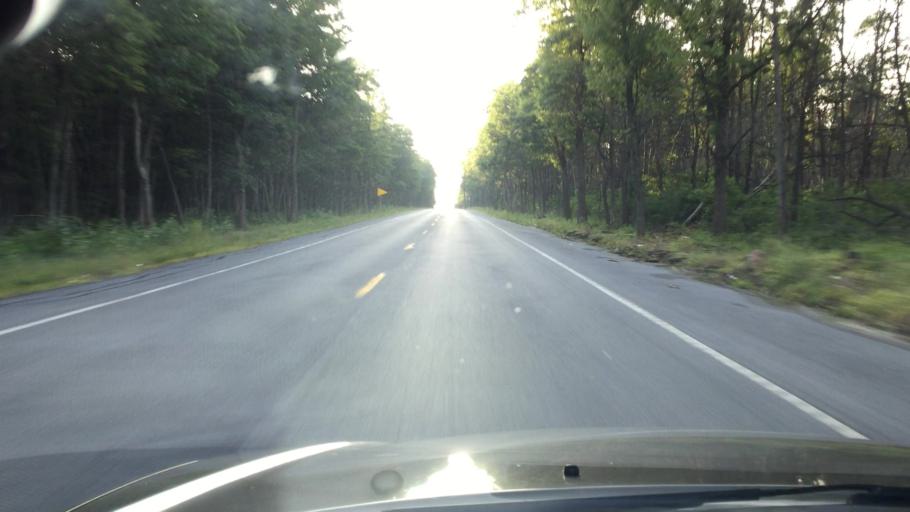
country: US
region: Pennsylvania
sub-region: Carbon County
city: Nesquehoning
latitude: 40.9002
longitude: -75.8168
